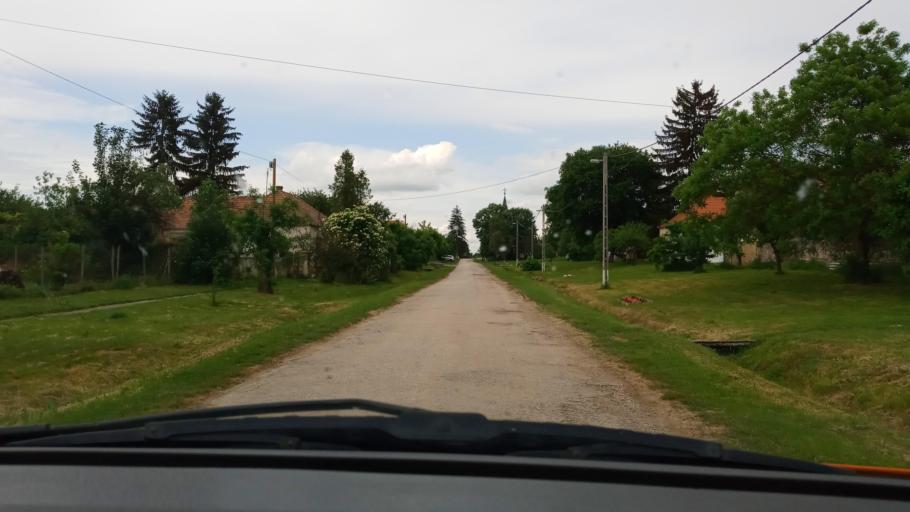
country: HU
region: Baranya
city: Harkany
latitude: 45.8975
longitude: 18.1365
